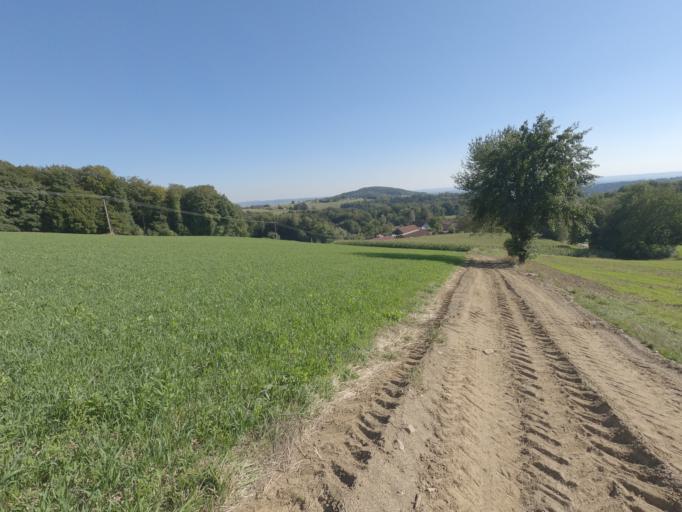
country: DE
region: Bavaria
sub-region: Lower Bavaria
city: Deggendorf
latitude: 48.8298
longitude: 13.0111
